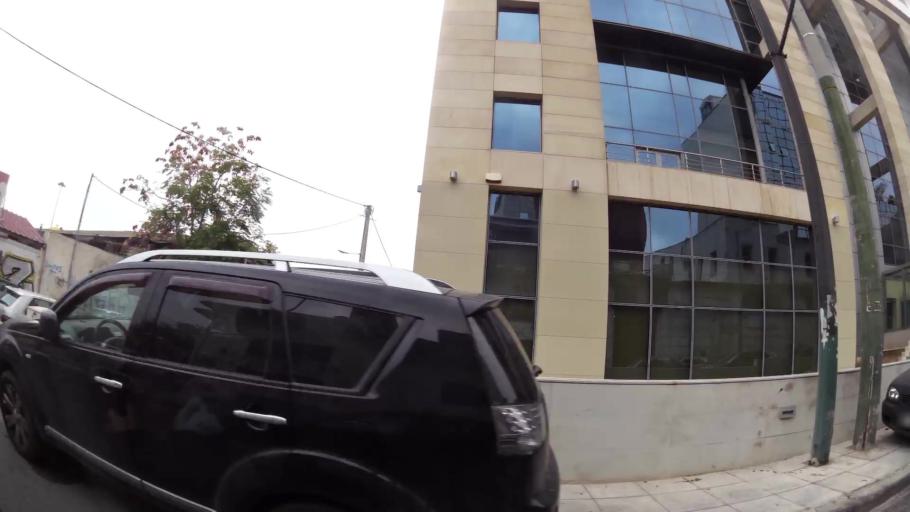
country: GR
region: Attica
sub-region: Nomos Attikis
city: Piraeus
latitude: 37.9501
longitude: 23.6386
